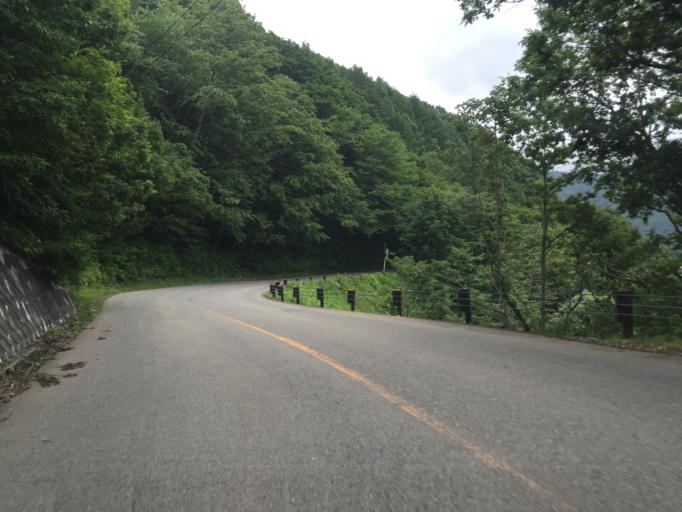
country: JP
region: Fukushima
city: Inawashiro
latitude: 37.7197
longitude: 140.0576
